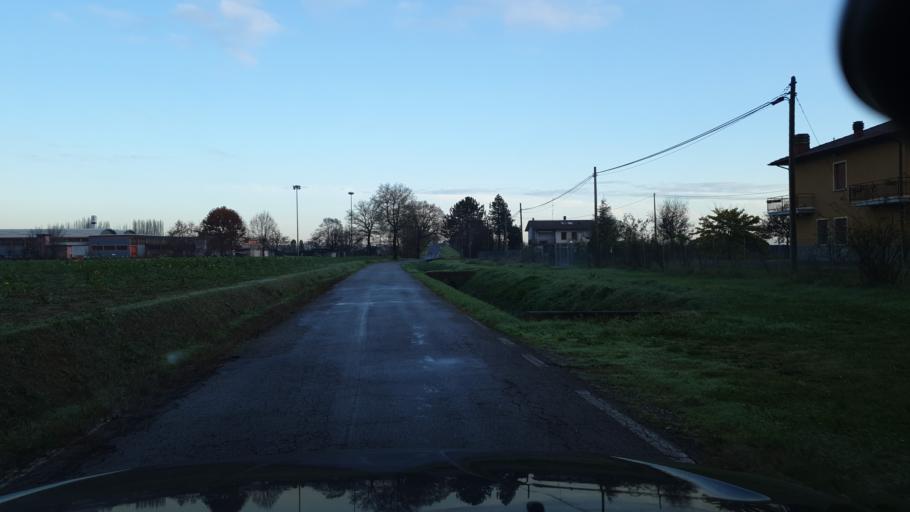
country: IT
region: Emilia-Romagna
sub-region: Provincia di Bologna
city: Crespellano
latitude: 44.5221
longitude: 11.1467
